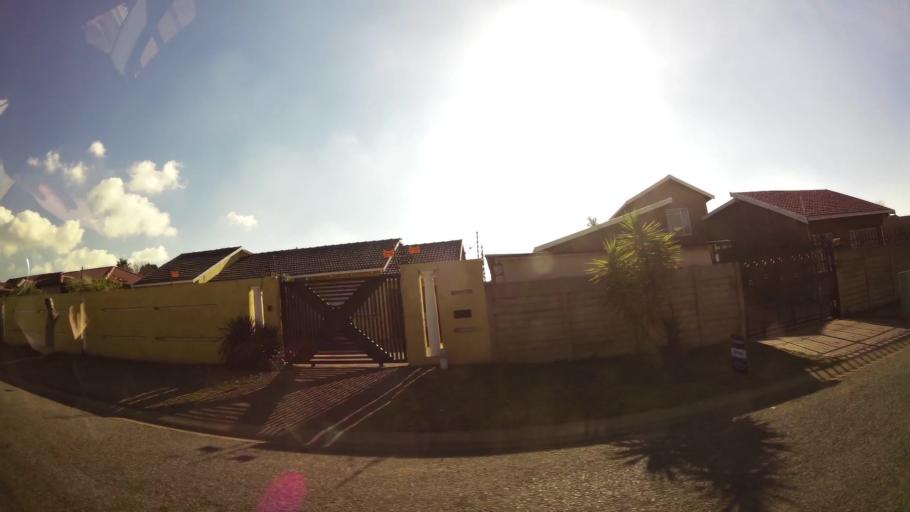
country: ZA
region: Gauteng
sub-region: City of Johannesburg Metropolitan Municipality
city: Roodepoort
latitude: -26.1644
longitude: 27.8172
